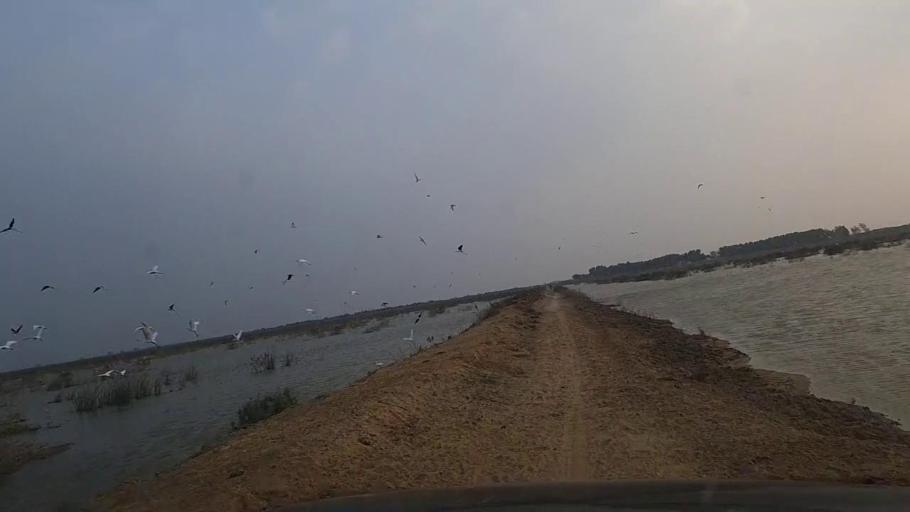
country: PK
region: Sindh
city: Gharo
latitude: 24.7685
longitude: 67.6918
